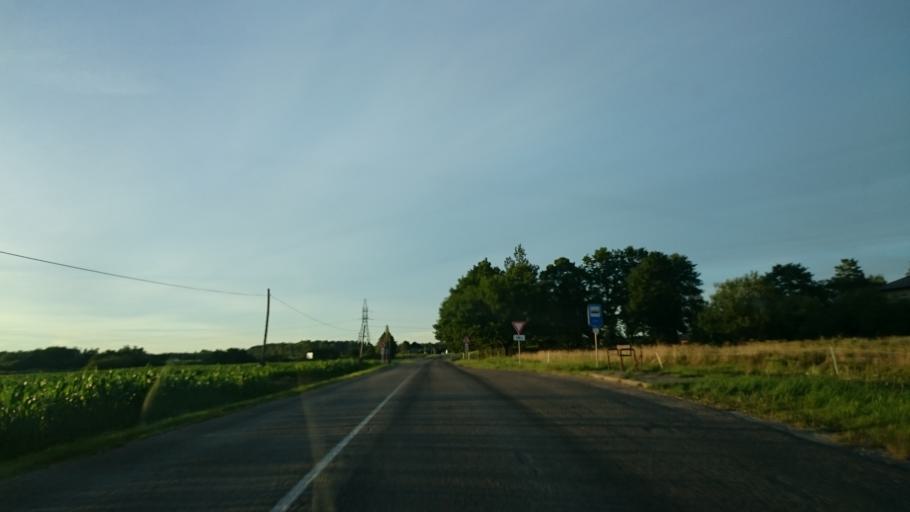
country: LV
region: Saldus Rajons
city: Saldus
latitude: 56.6866
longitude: 22.5044
